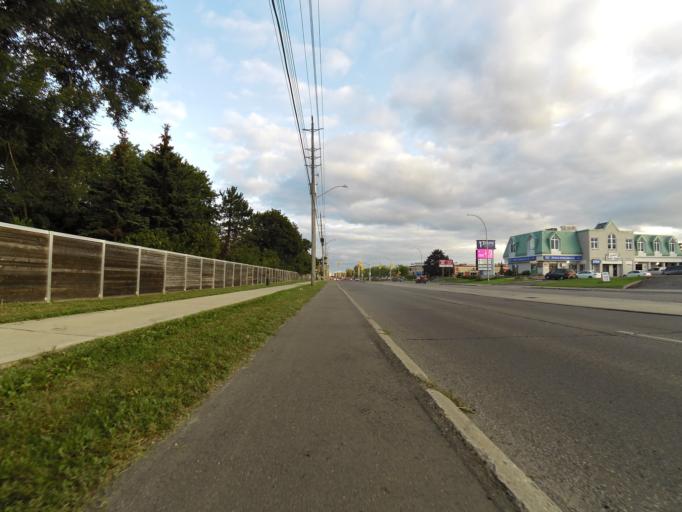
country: CA
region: Ontario
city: Bells Corners
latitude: 45.2871
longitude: -75.7563
